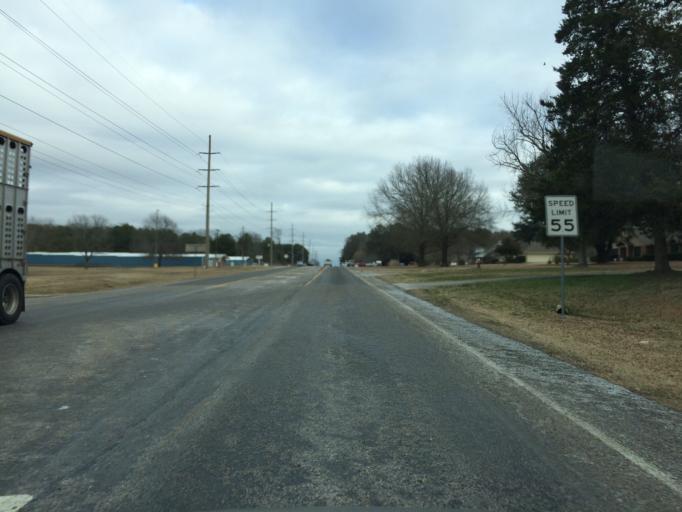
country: US
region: Texas
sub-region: Wood County
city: Mineola
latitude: 32.6880
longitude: -95.4828
